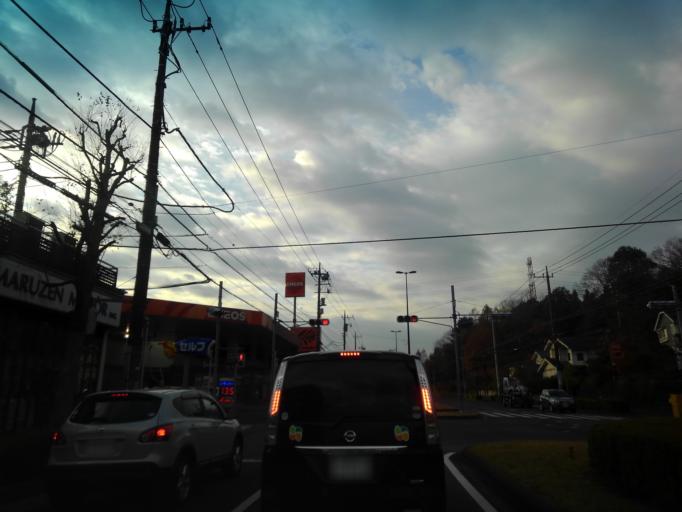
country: JP
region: Tokyo
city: Hino
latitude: 35.6277
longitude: 139.4424
